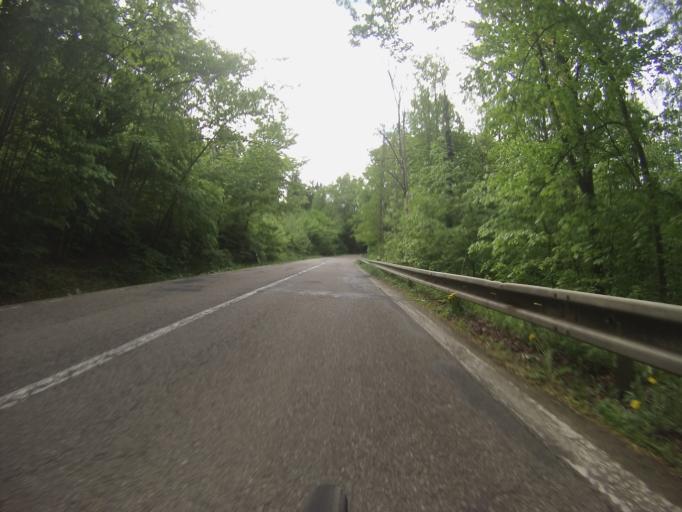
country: CZ
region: South Moravian
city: Veverska Bityska
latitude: 49.2524
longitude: 16.4804
